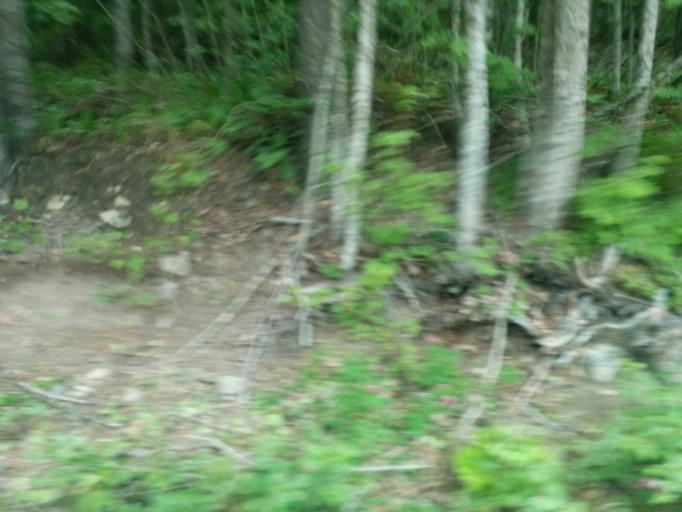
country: FI
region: Pirkanmaa
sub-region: Tampere
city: Kuhmalahti
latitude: 61.6838
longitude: 24.5656
